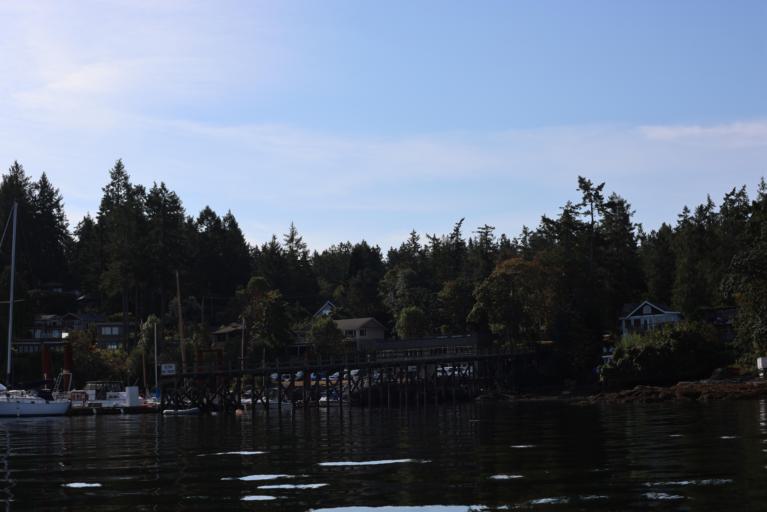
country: CA
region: British Columbia
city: North Saanich
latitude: 48.6806
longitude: -123.4789
